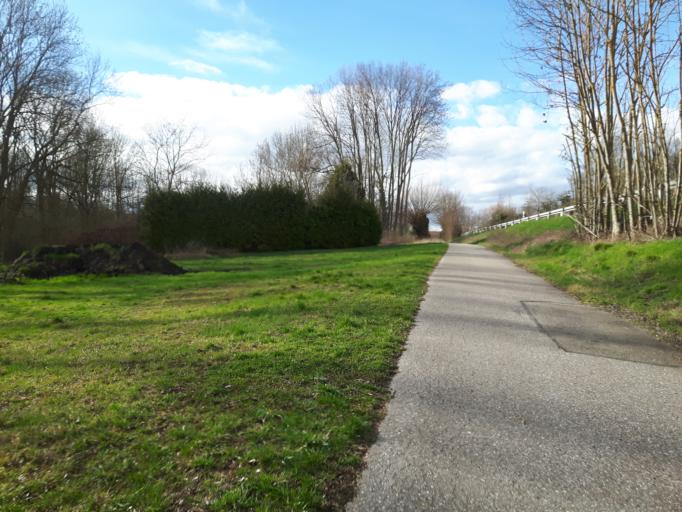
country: DE
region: Baden-Wuerttemberg
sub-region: Regierungsbezirk Stuttgart
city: Bonnigheim
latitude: 49.0698
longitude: 9.1065
